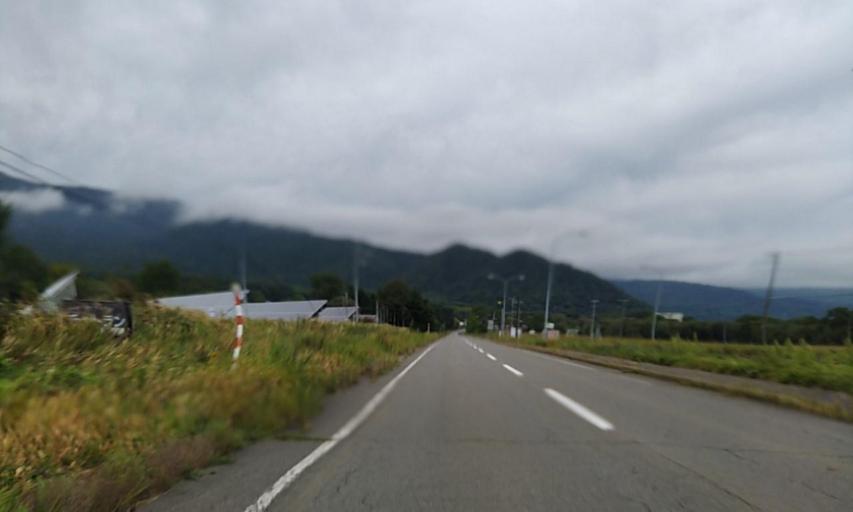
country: JP
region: Hokkaido
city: Bihoro
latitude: 43.5793
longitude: 144.2814
